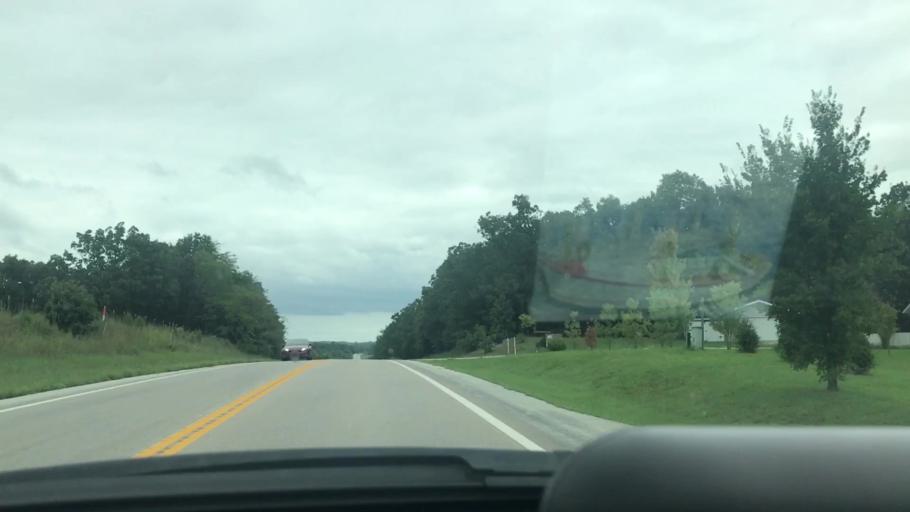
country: US
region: Missouri
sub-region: Dallas County
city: Buffalo
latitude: 37.7126
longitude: -93.1162
